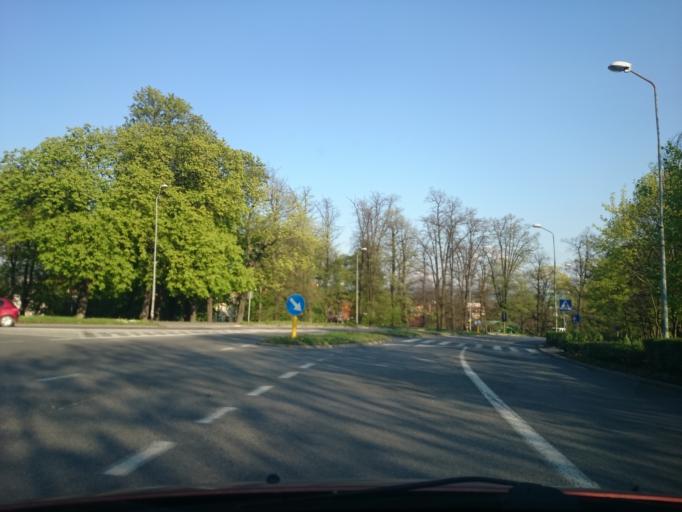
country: PL
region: Lower Silesian Voivodeship
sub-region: Powiat klodzki
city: Klodzko
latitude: 50.4395
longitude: 16.6480
